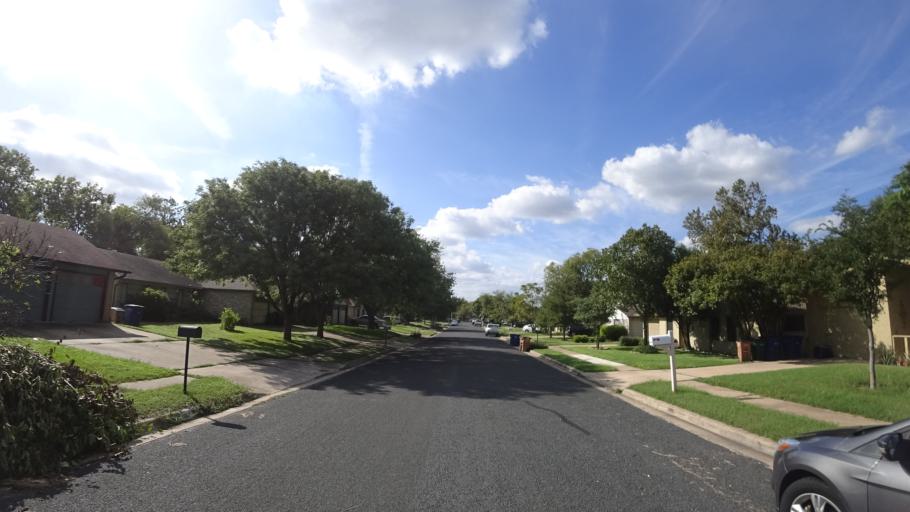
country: US
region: Texas
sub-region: Travis County
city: Onion Creek
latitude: 30.2025
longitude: -97.7942
